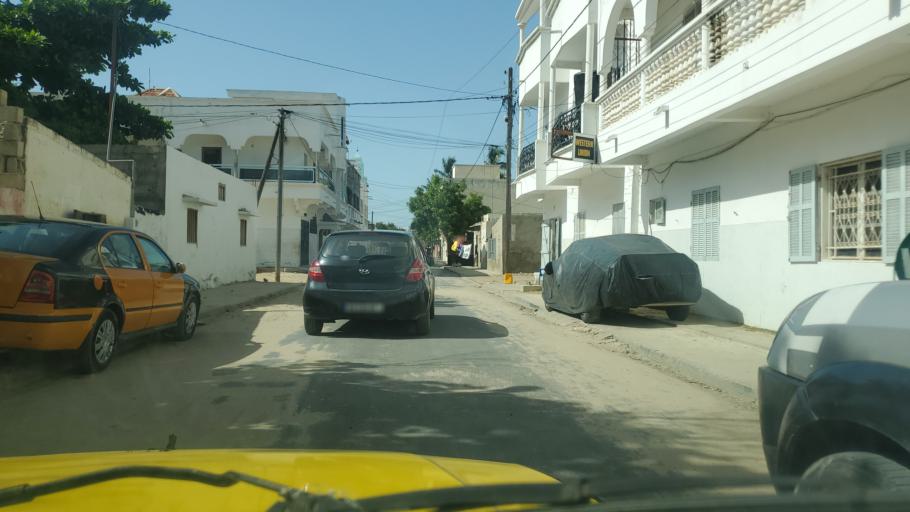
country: SN
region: Saint-Louis
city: Saint-Louis
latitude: 16.0200
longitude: -16.4855
